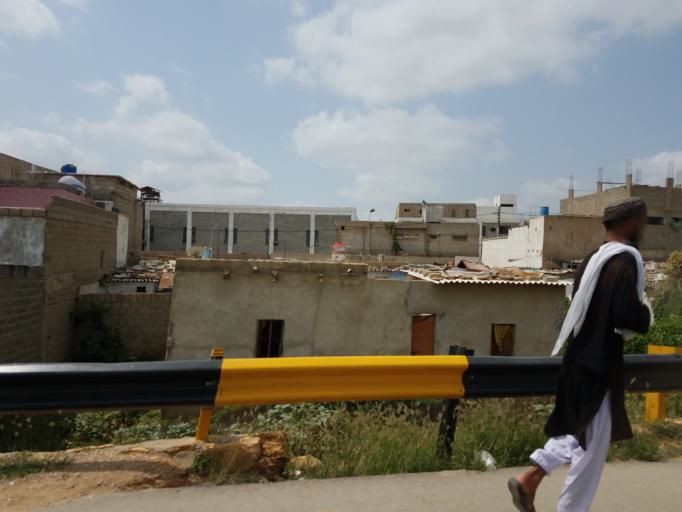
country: PK
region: Sindh
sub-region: Karachi District
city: Karachi
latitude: 24.9409
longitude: 67.0889
